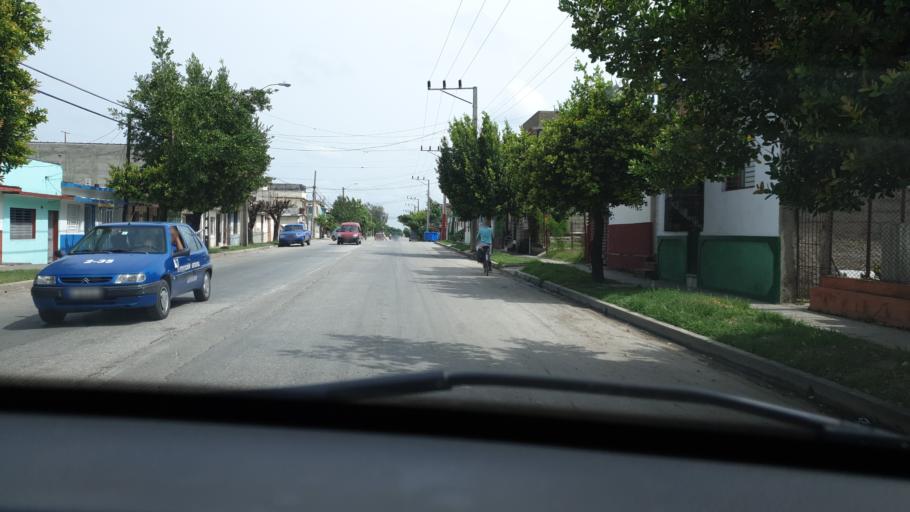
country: CU
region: Villa Clara
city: Santa Clara
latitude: 22.3886
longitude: -79.9595
